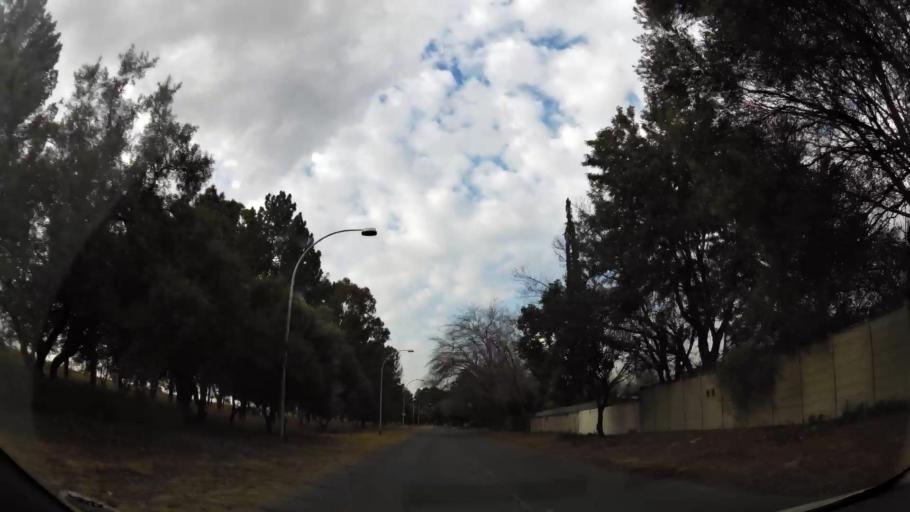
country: ZA
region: Orange Free State
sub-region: Fezile Dabi District Municipality
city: Sasolburg
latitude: -26.7908
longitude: 27.8173
